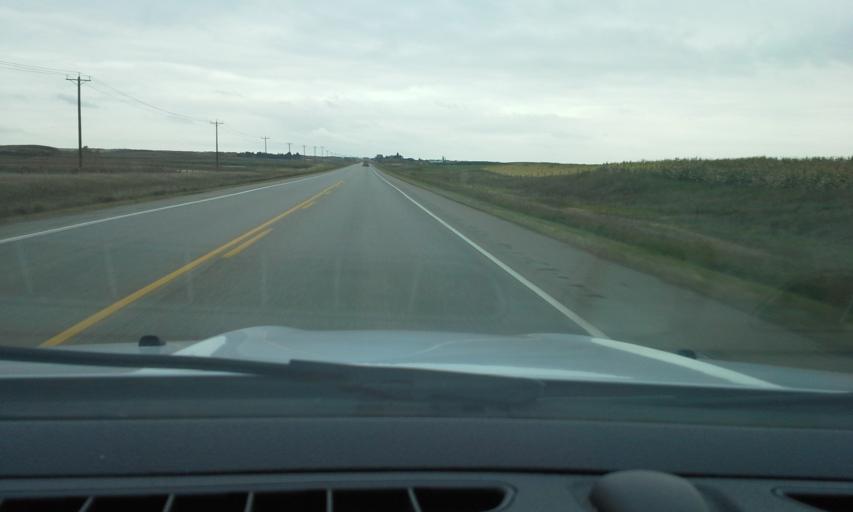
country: CA
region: Saskatchewan
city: Lloydminster
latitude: 53.2779
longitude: -109.8783
